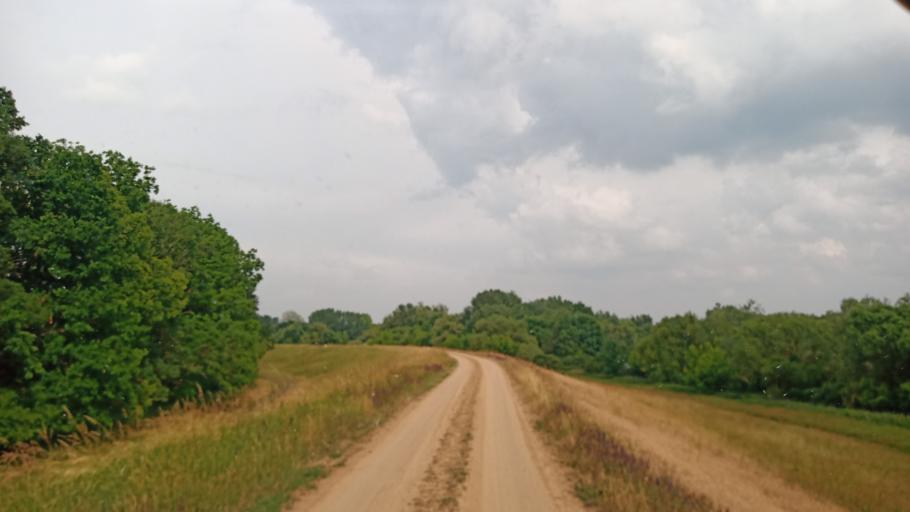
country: HU
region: Bekes
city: Doboz
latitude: 46.7071
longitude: 21.2986
